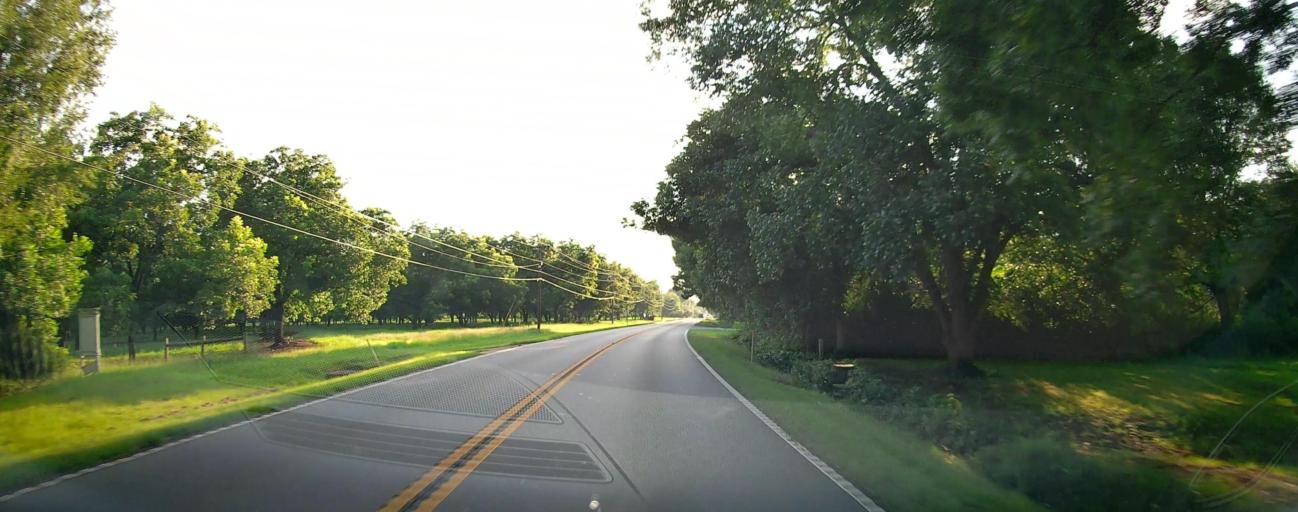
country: US
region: Georgia
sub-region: Peach County
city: Fort Valley
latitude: 32.5577
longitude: -83.9031
